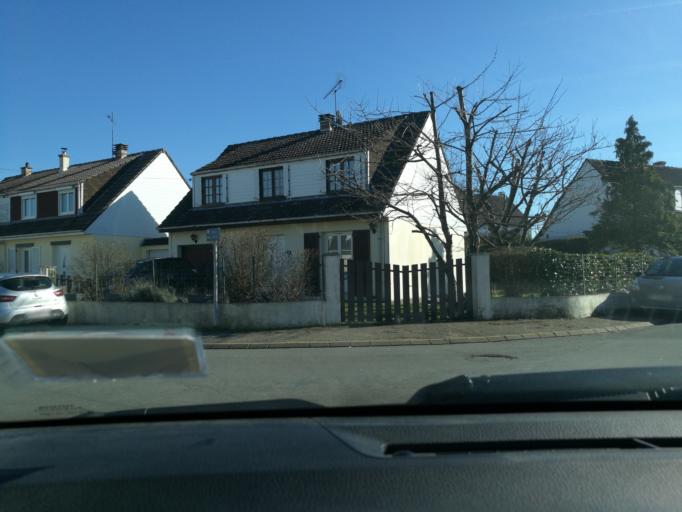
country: FR
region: Centre
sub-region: Departement du Loiret
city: Saint-Ay
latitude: 47.8674
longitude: 1.7649
